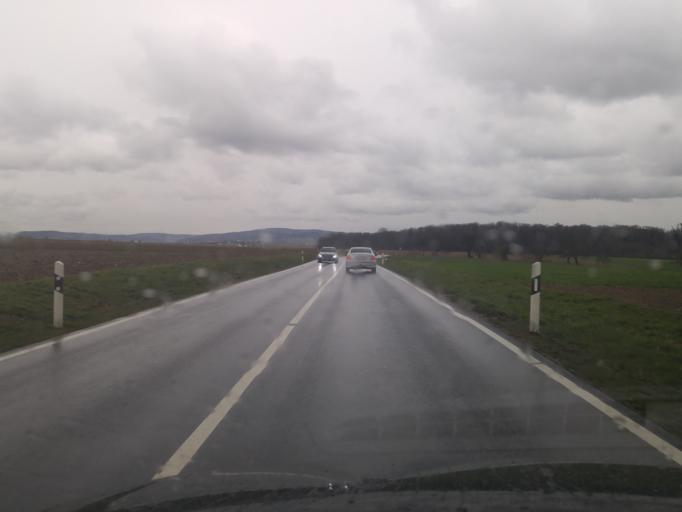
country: DE
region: Baden-Wuerttemberg
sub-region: Regierungsbezirk Stuttgart
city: Affalterbach
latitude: 48.9106
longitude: 9.3390
